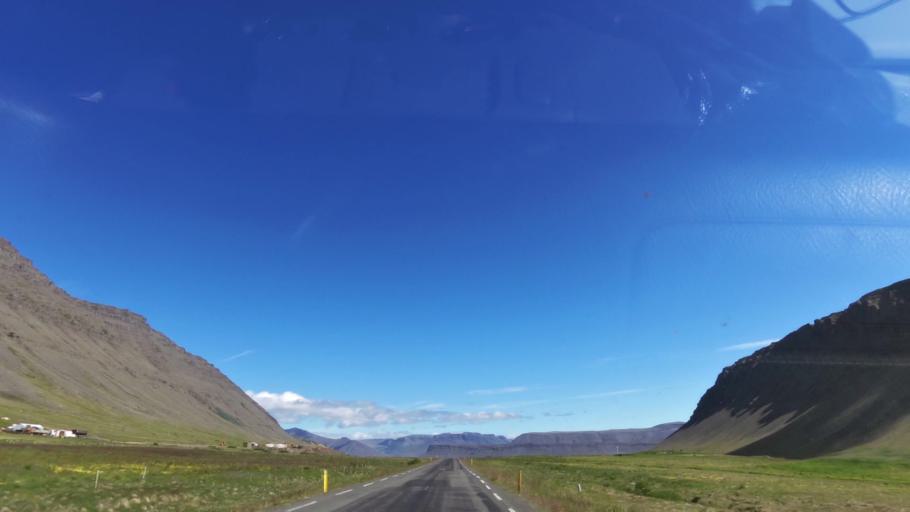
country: IS
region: Westfjords
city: Isafjoerdur
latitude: 65.6699
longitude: -23.6274
